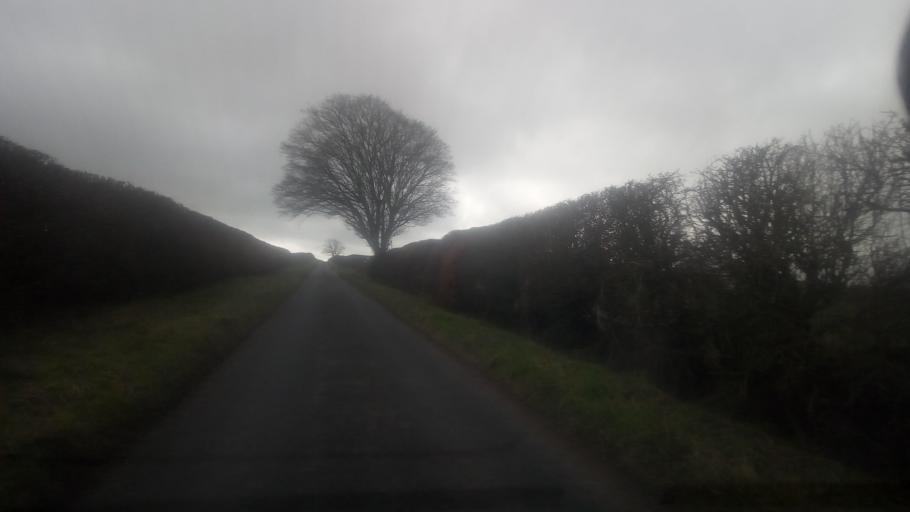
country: GB
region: Scotland
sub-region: The Scottish Borders
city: Jedburgh
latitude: 55.4962
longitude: -2.5152
